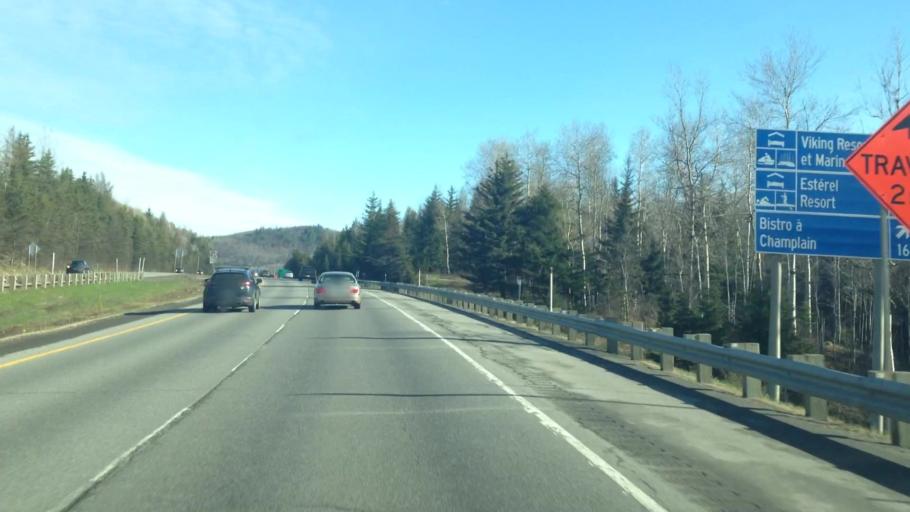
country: CA
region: Quebec
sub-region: Laurentides
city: Sainte-Adele
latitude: 45.9476
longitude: -74.1247
